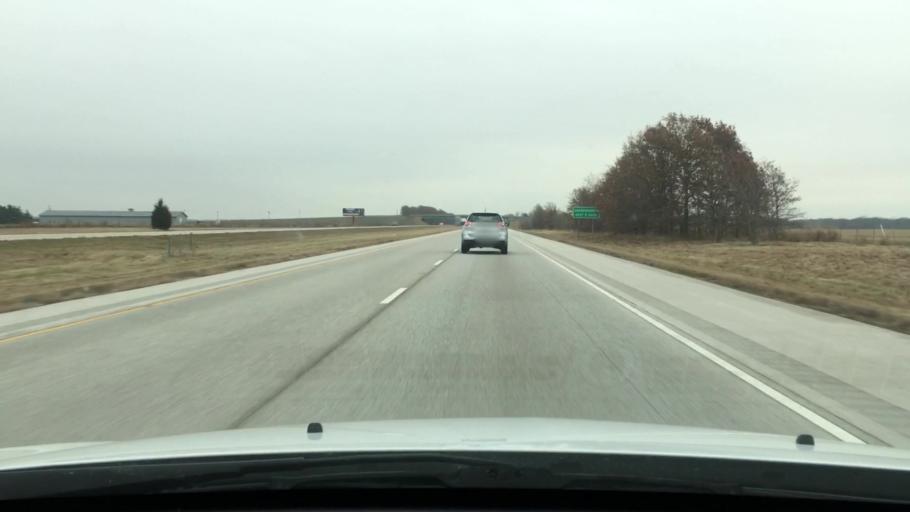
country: US
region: Illinois
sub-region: Morgan County
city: South Jacksonville
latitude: 39.6802
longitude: -90.3336
